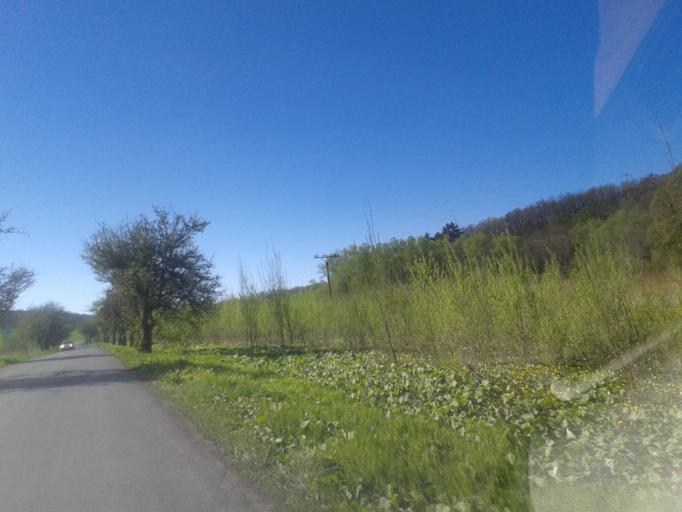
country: CZ
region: Central Bohemia
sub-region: Okres Beroun
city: Beroun
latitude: 49.9098
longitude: 14.1004
